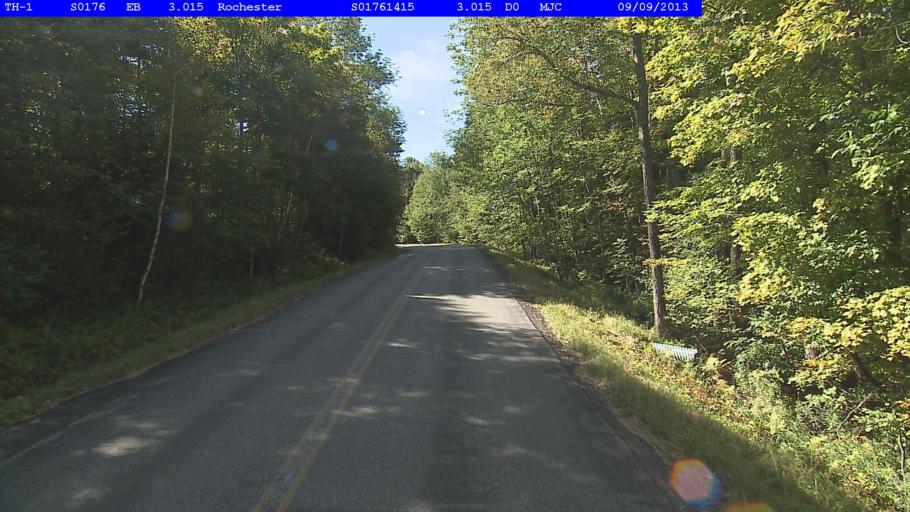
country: US
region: Vermont
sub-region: Orange County
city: Randolph
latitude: 43.8612
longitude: -72.7620
